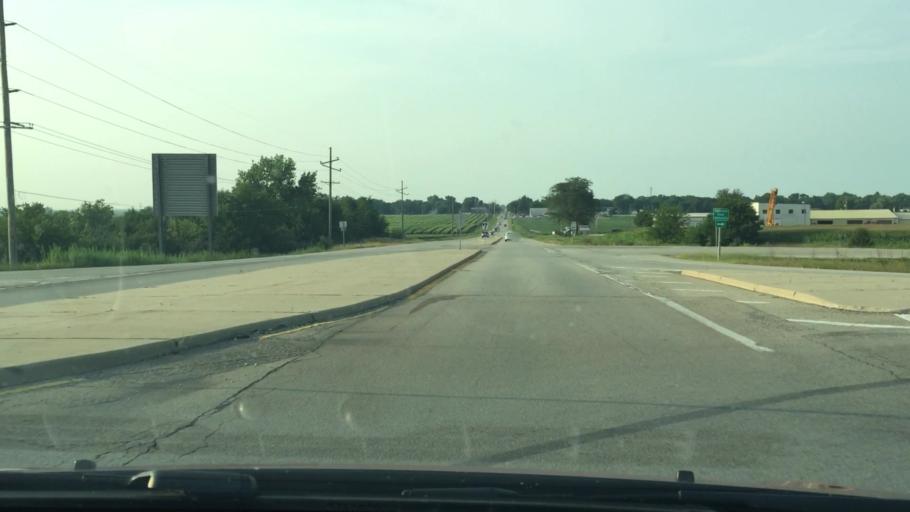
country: US
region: Illinois
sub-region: Bureau County
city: Ladd
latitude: 41.3696
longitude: -89.2189
